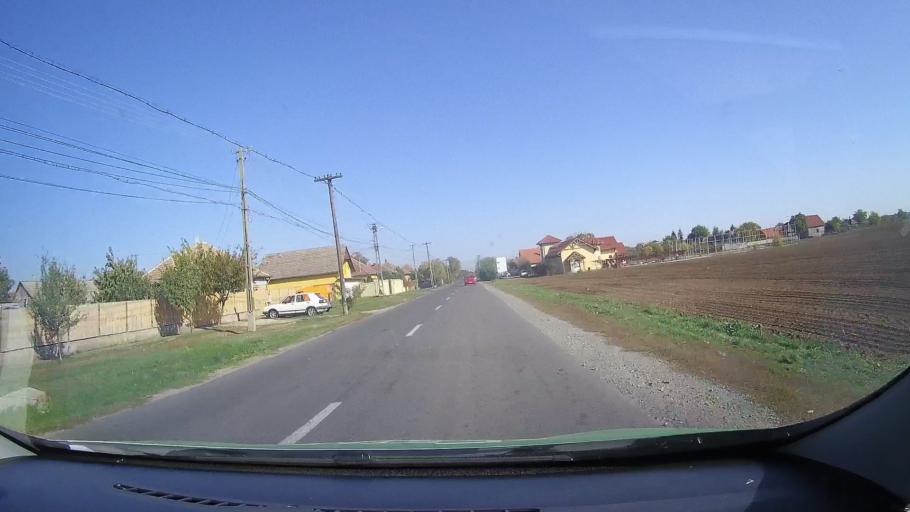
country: RO
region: Satu Mare
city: Carei
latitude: 47.6717
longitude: 22.4661
